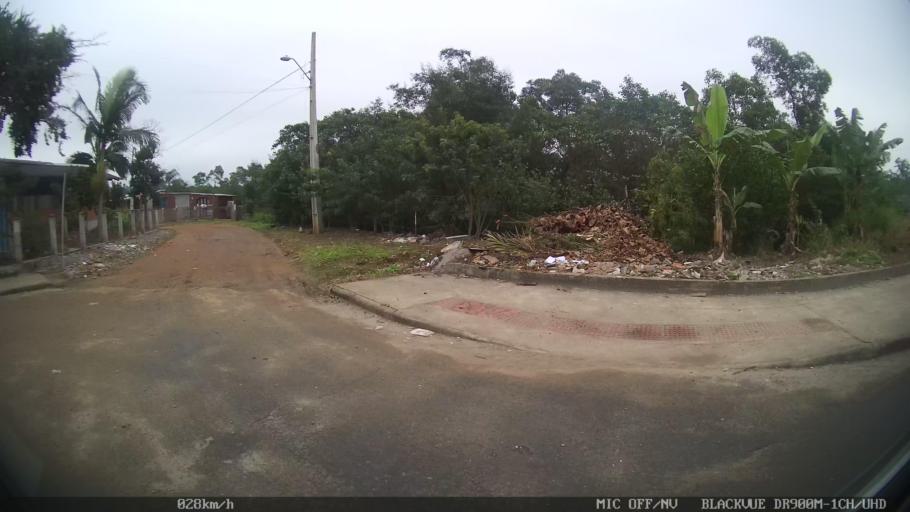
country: BR
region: Santa Catarina
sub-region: Joinville
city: Joinville
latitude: -26.2558
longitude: -48.8024
